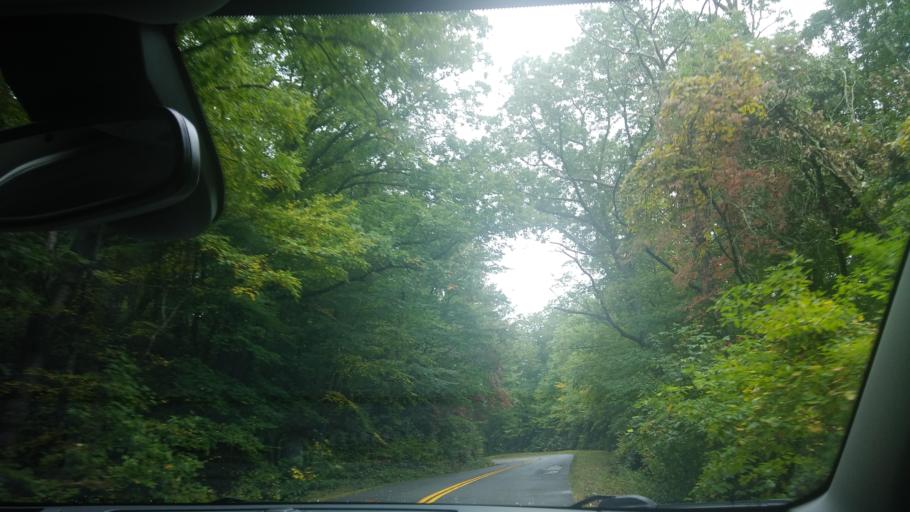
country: US
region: North Carolina
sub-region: Mitchell County
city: Spruce Pine
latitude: 35.9065
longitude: -81.9762
